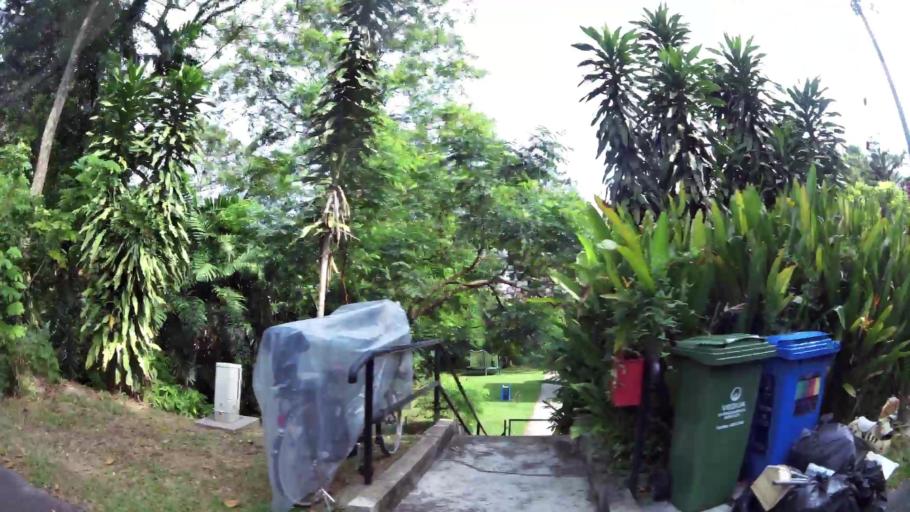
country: SG
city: Singapore
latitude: 1.2943
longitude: 103.7978
